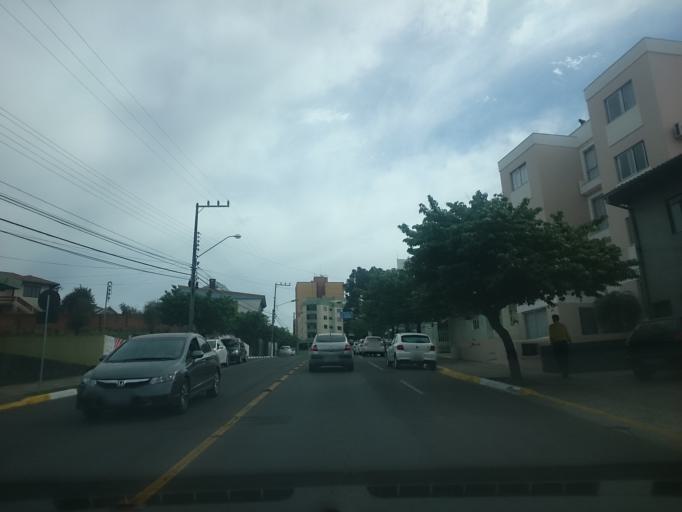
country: BR
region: Santa Catarina
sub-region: Lages
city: Lages
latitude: -27.8195
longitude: -50.3228
